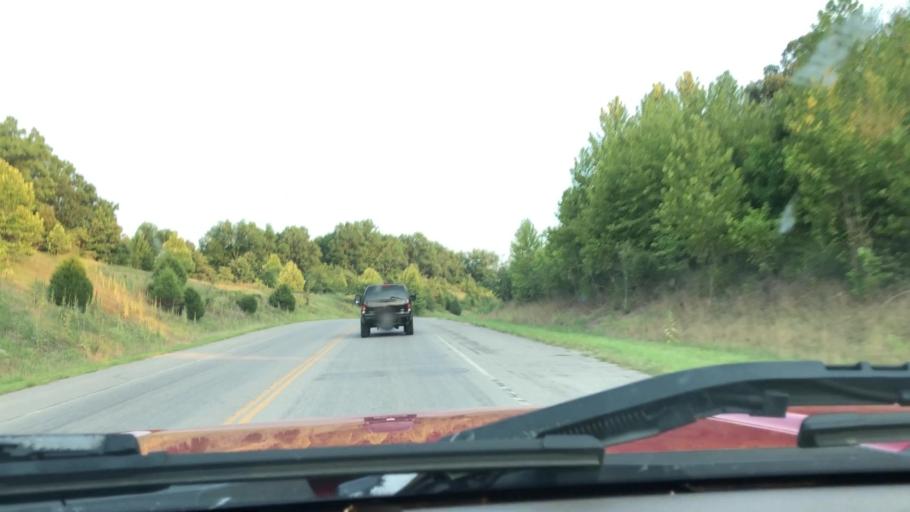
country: US
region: Missouri
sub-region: Jasper County
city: Joplin
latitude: 37.0247
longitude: -94.5144
